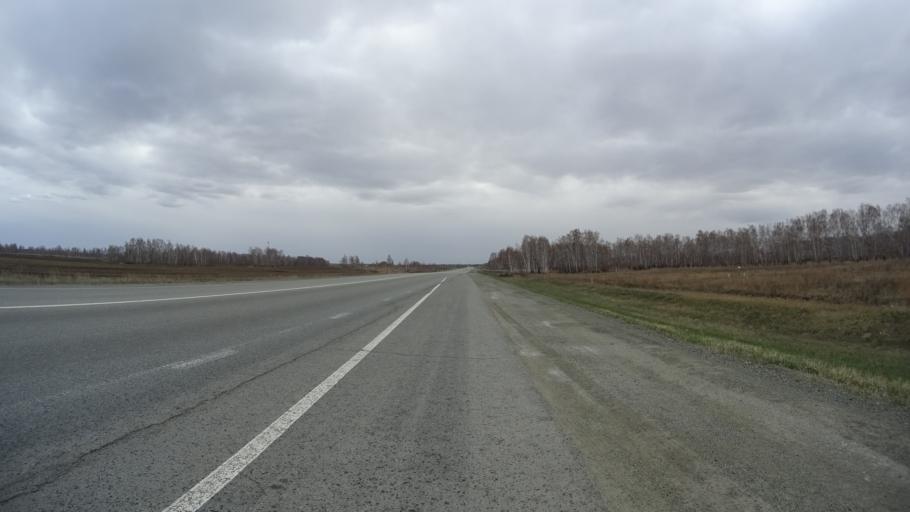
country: RU
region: Chelyabinsk
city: Yemanzhelinsk
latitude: 54.6949
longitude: 61.2496
